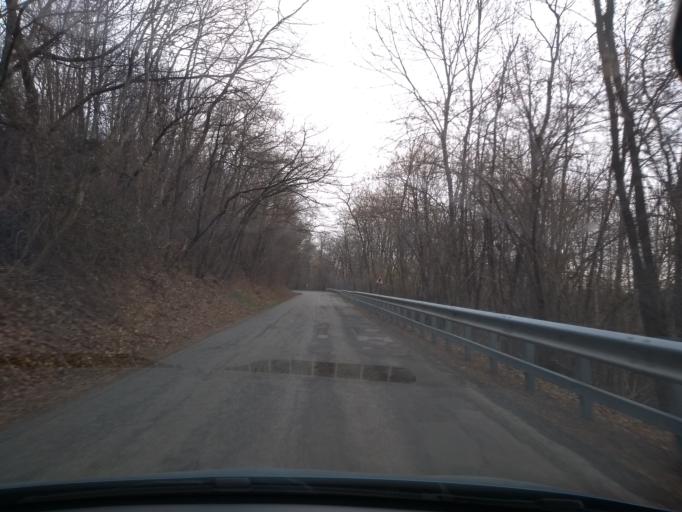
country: IT
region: Piedmont
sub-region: Provincia di Biella
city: Zubiena
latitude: 45.4870
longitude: 7.9804
